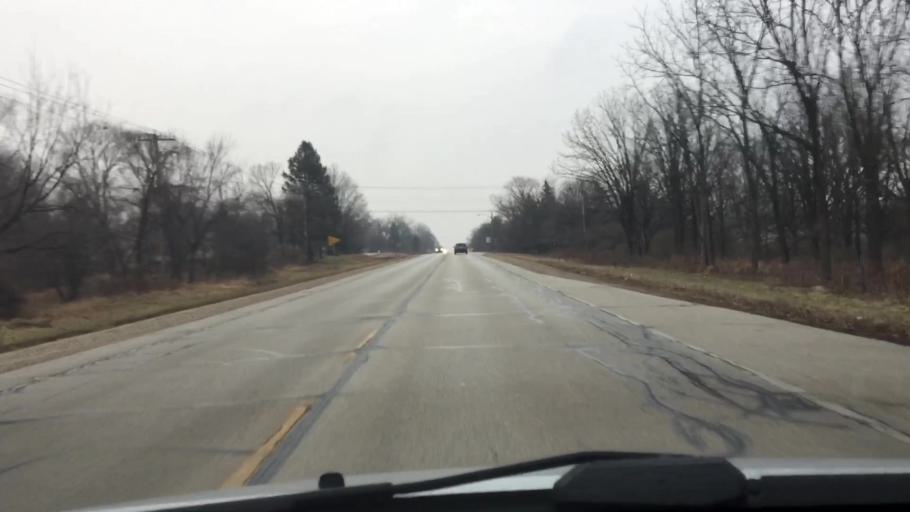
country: US
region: Wisconsin
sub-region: Waukesha County
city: Waukesha
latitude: 43.0209
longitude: -88.2772
